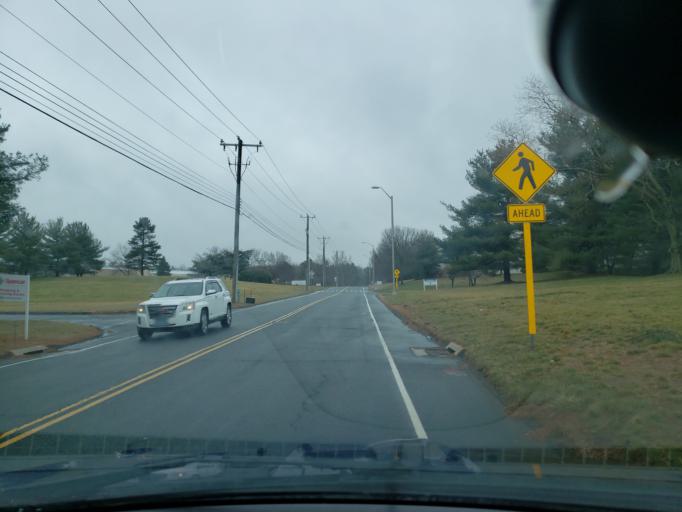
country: US
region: Connecticut
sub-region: Hartford County
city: Windsor
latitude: 41.8766
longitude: -72.6870
